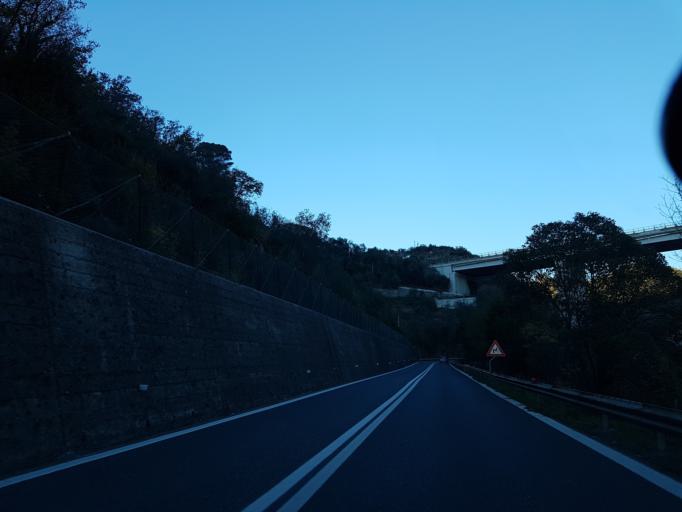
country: IT
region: Liguria
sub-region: Provincia di Genova
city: Recco
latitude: 44.3727
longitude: 9.1490
